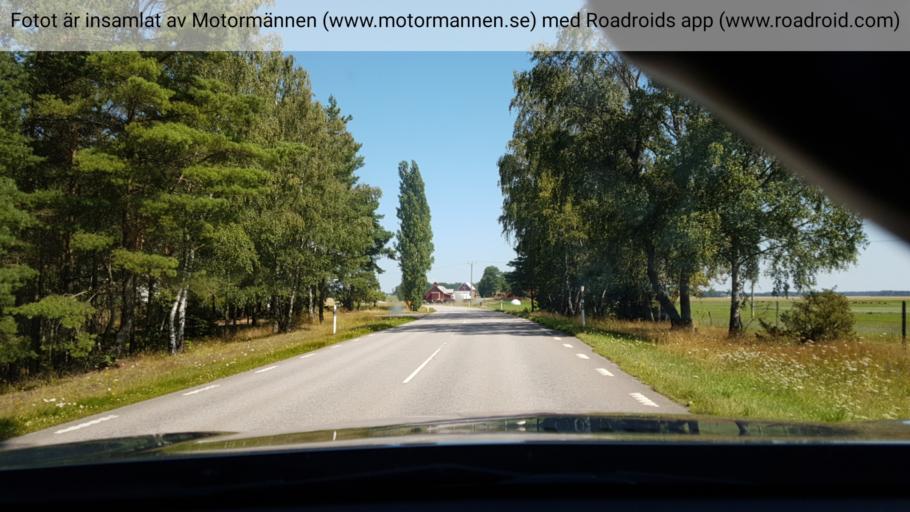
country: SE
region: Vaestra Goetaland
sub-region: Vara Kommun
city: Vara
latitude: 58.3648
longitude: 12.9619
